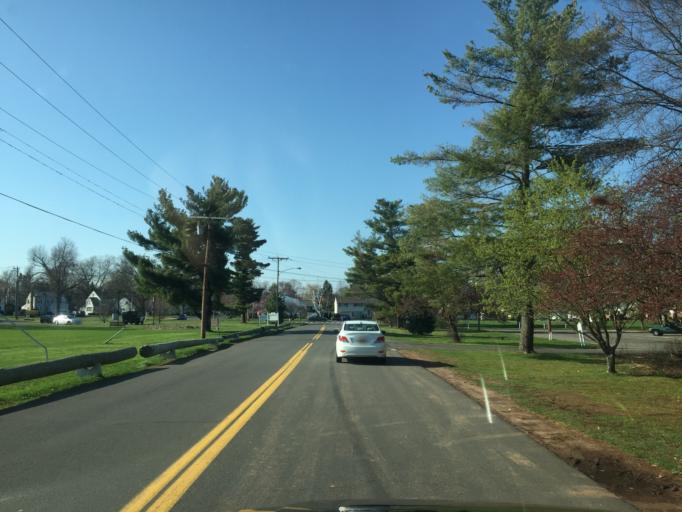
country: US
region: Connecticut
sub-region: Hartford County
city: Wethersfield
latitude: 41.6932
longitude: -72.6667
